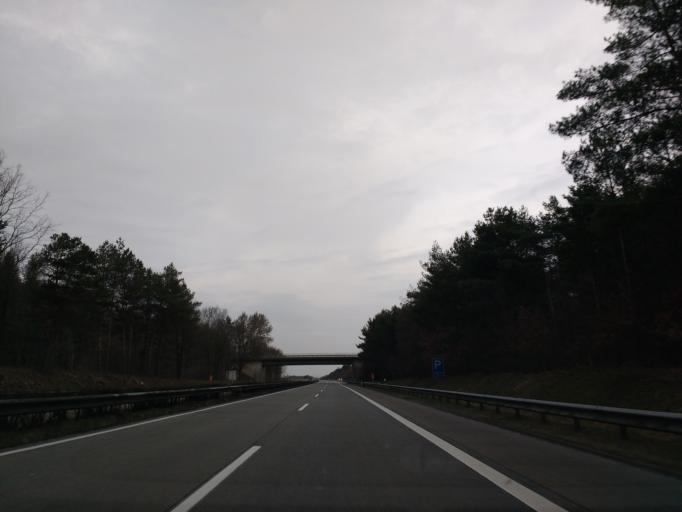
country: DE
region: Lower Saxony
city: Midlum
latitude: 53.7053
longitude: 8.6637
